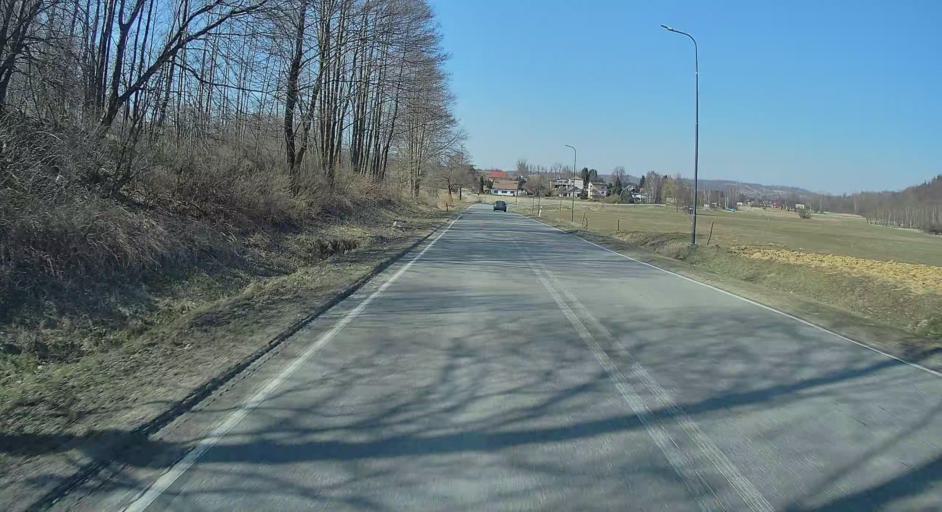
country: PL
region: Subcarpathian Voivodeship
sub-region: Powiat rzeszowski
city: Blazowa
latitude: 49.9315
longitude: 22.1165
